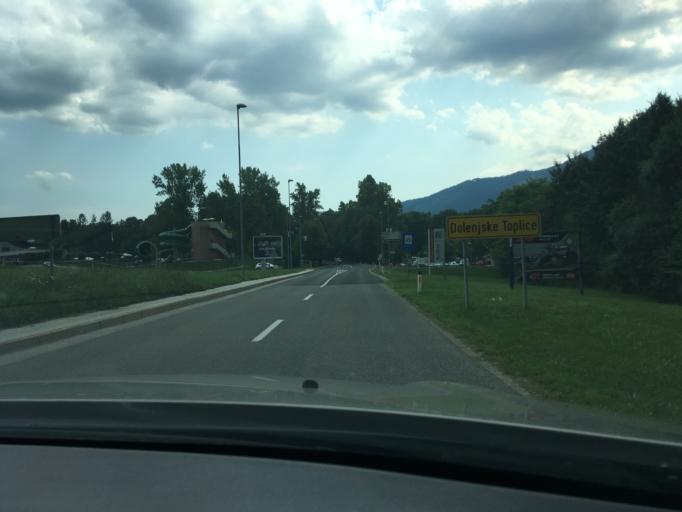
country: SI
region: Dolenjske Toplice
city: Dolenjske Toplice
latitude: 45.7612
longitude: 15.0573
